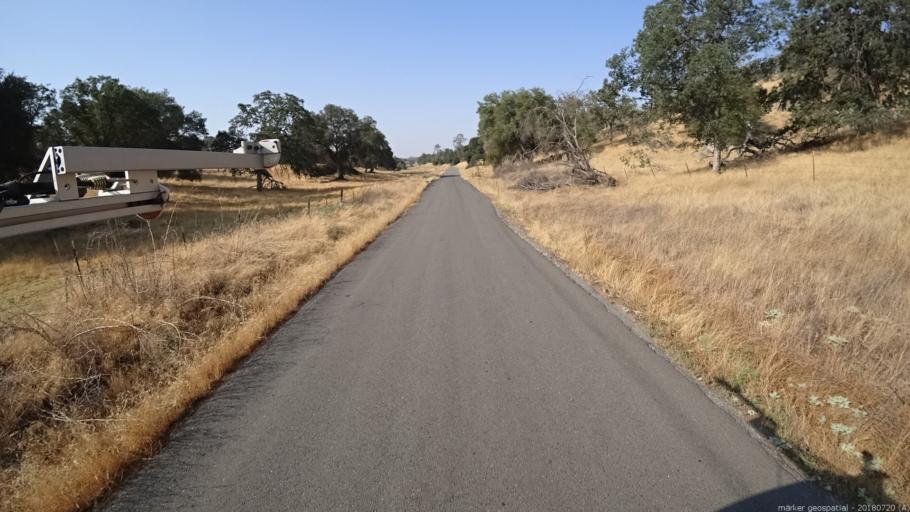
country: US
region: California
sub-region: Madera County
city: Yosemite Lakes
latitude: 37.2366
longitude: -119.9063
